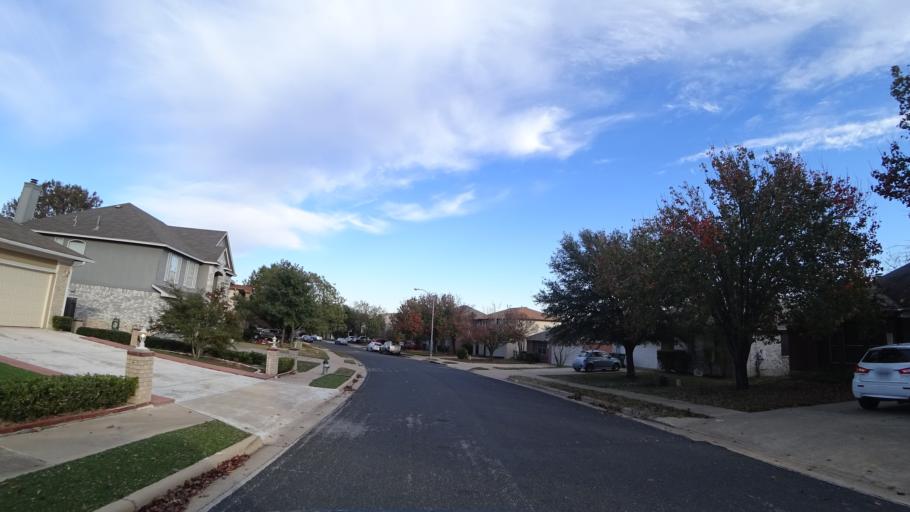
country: US
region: Texas
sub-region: Williamson County
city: Brushy Creek
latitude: 30.4997
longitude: -97.7307
